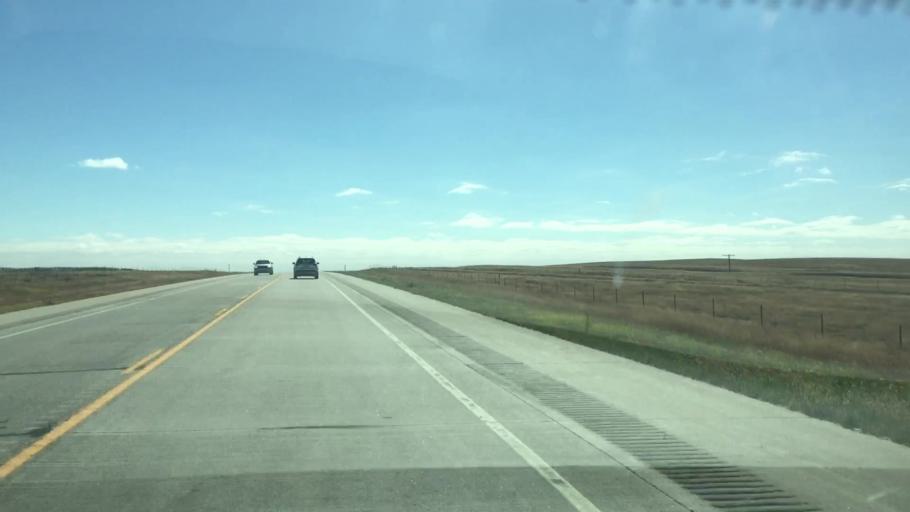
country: US
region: Colorado
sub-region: Lincoln County
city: Hugo
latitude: 39.1768
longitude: -103.5409
